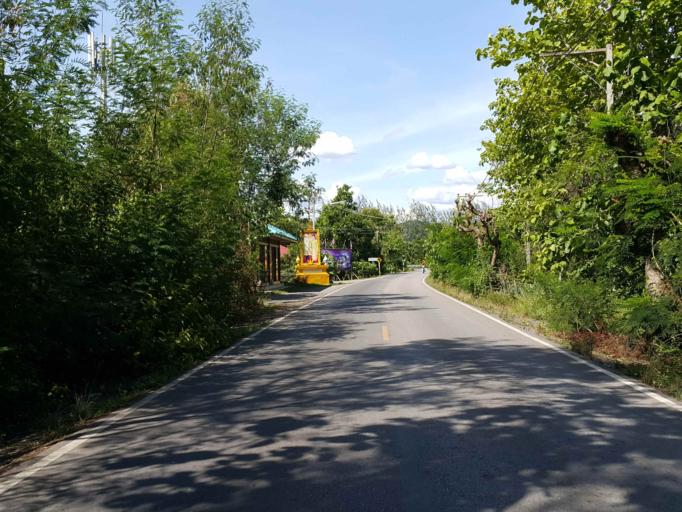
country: TH
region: Chiang Mai
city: San Kamphaeng
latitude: 18.7721
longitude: 99.1540
